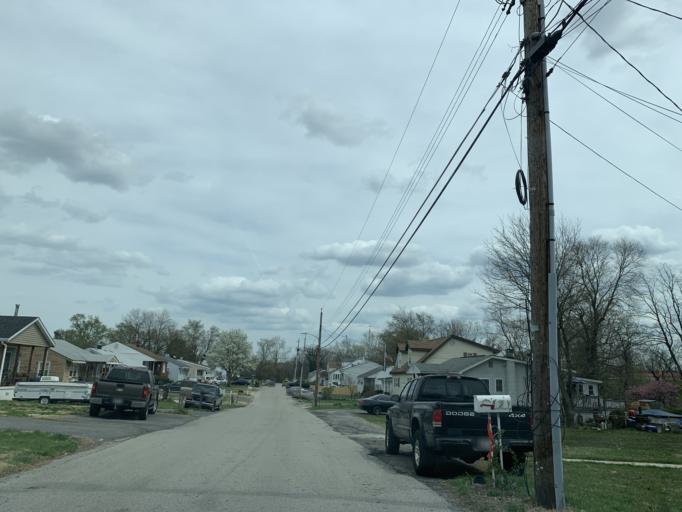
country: US
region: Maryland
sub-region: Baltimore County
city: Baltimore Highlands
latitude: 39.2316
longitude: -76.6397
